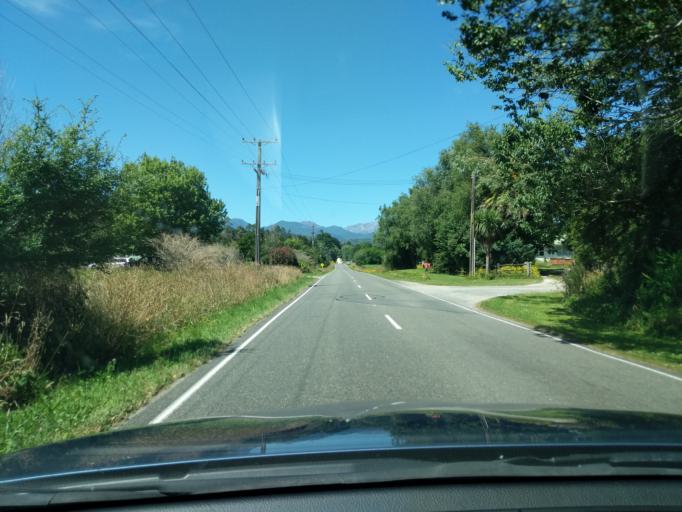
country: NZ
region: Tasman
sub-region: Tasman District
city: Takaka
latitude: -40.7255
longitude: 172.6378
